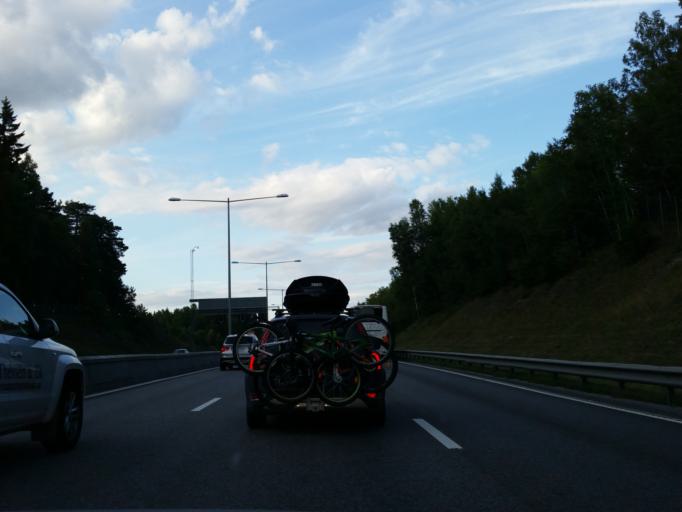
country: SE
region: Stockholm
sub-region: Botkyrka Kommun
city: Eriksberg
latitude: 59.2209
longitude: 17.7834
